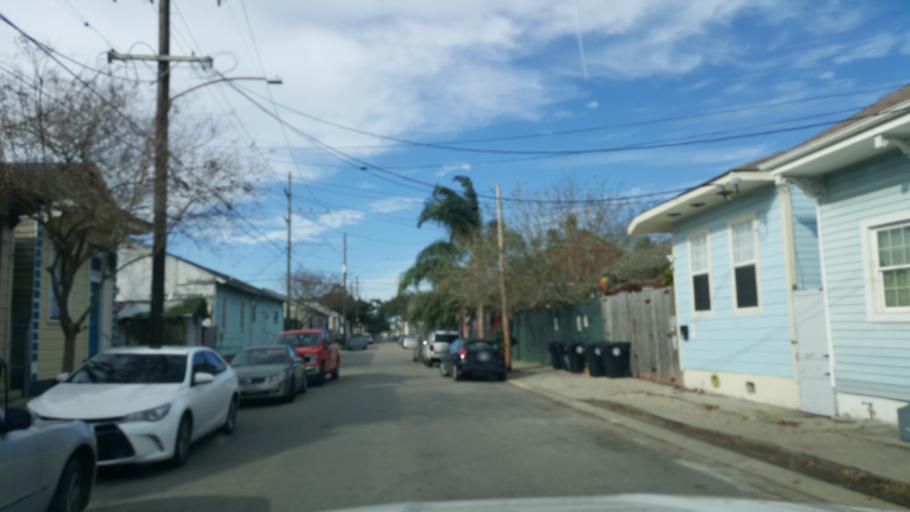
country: US
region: Louisiana
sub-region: Orleans Parish
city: New Orleans
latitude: 29.9706
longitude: -90.0550
